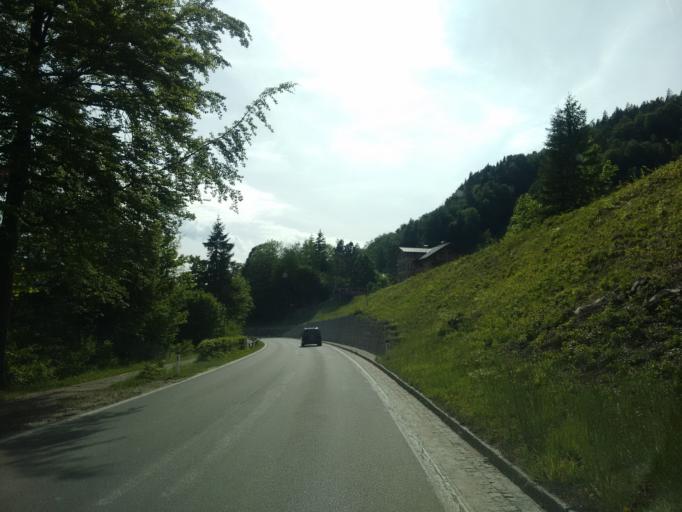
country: AT
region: Styria
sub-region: Politischer Bezirk Liezen
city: Bad Aussee
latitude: 47.6344
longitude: 13.8539
